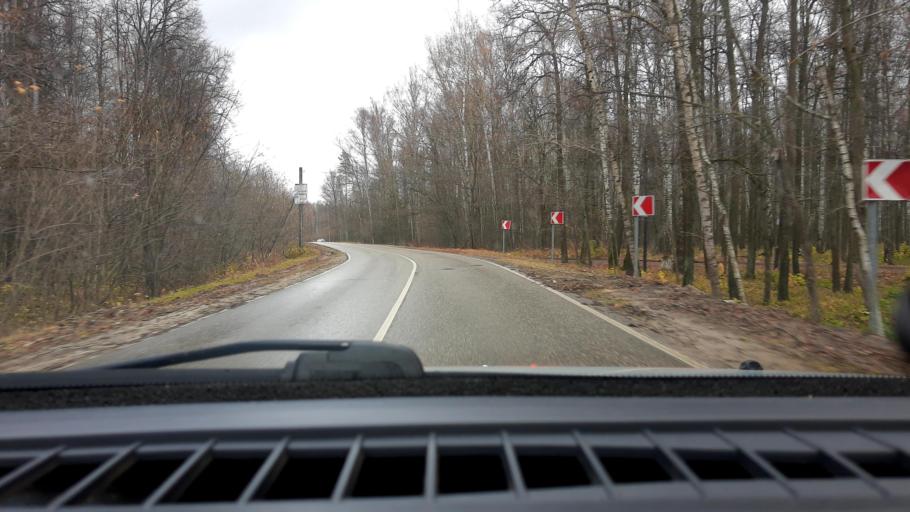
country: RU
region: Nizjnij Novgorod
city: Afonino
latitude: 56.1889
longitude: 44.0248
